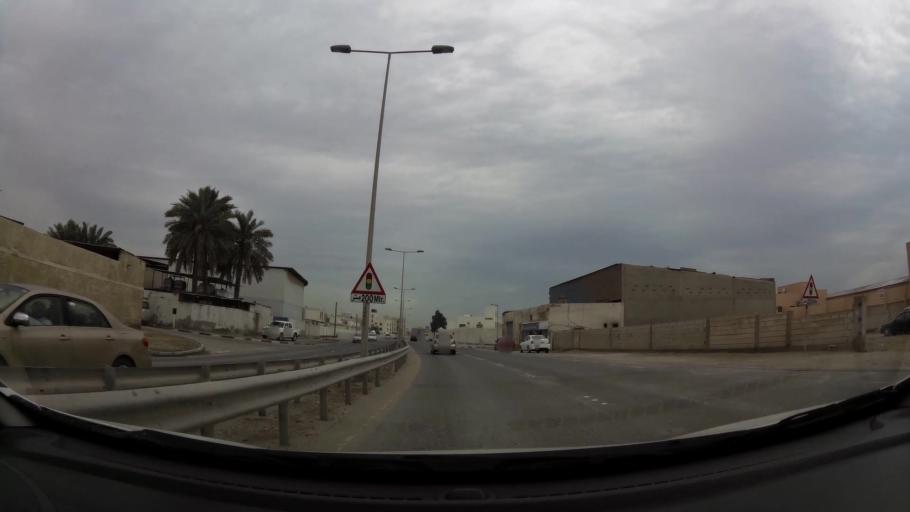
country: BH
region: Northern
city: Sitrah
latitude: 26.1542
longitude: 50.6204
